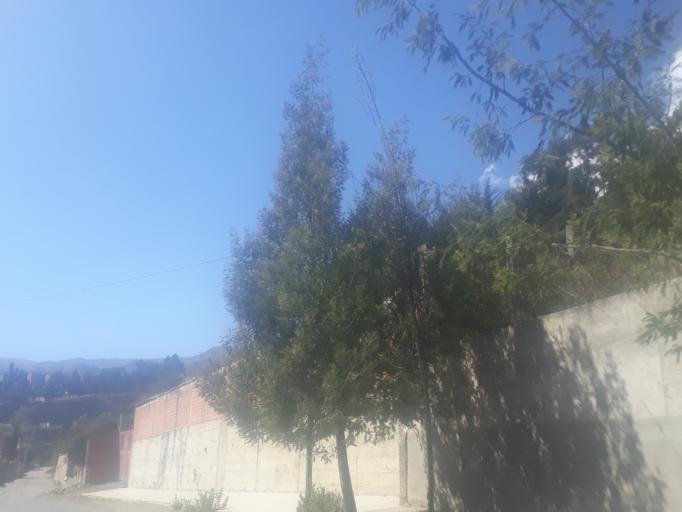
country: BO
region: La Paz
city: La Paz
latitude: -16.5377
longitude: -68.0554
